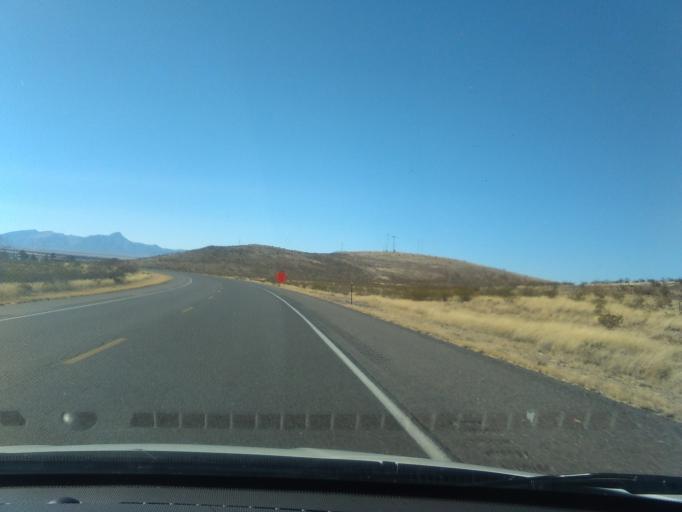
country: US
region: New Mexico
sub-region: Dona Ana County
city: Hatch
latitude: 32.5780
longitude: -107.4441
